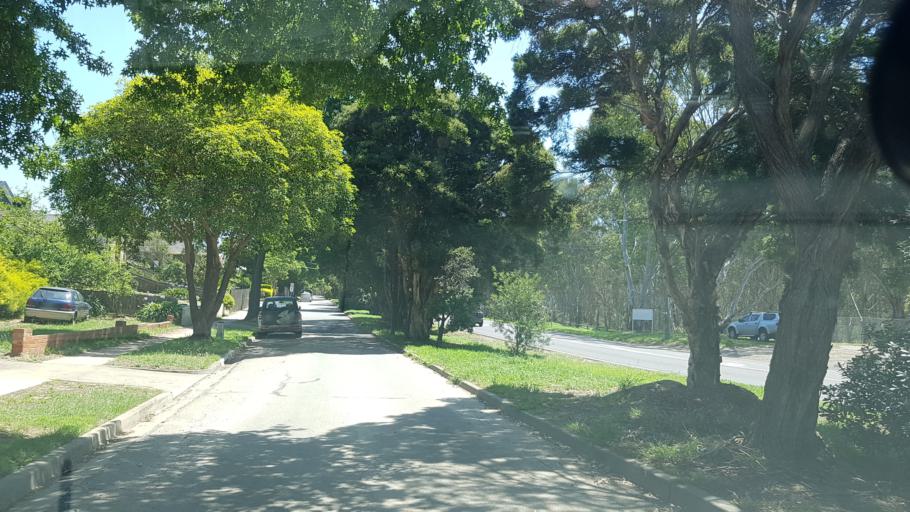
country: AU
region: Victoria
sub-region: Banyule
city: Viewbank
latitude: -37.7563
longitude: 145.0996
